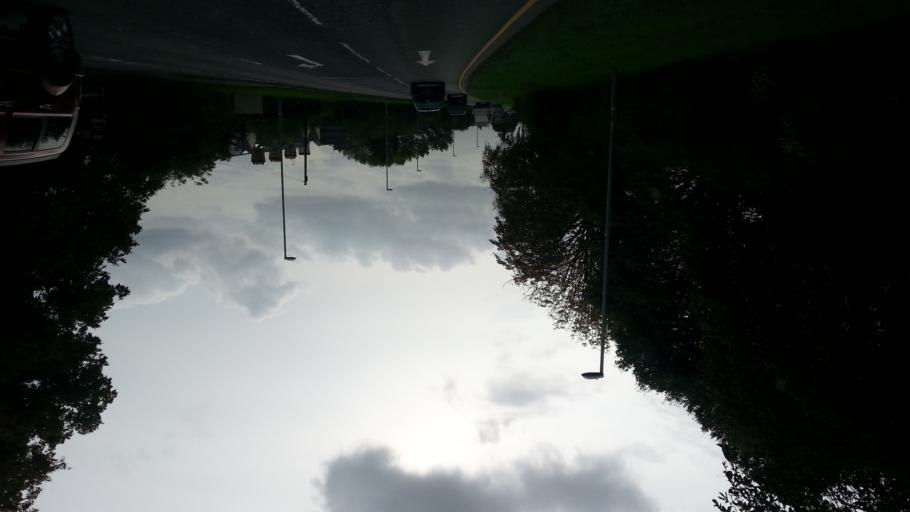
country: GB
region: England
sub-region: Cambridgeshire
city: Duxford
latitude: 52.0945
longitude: 0.1268
